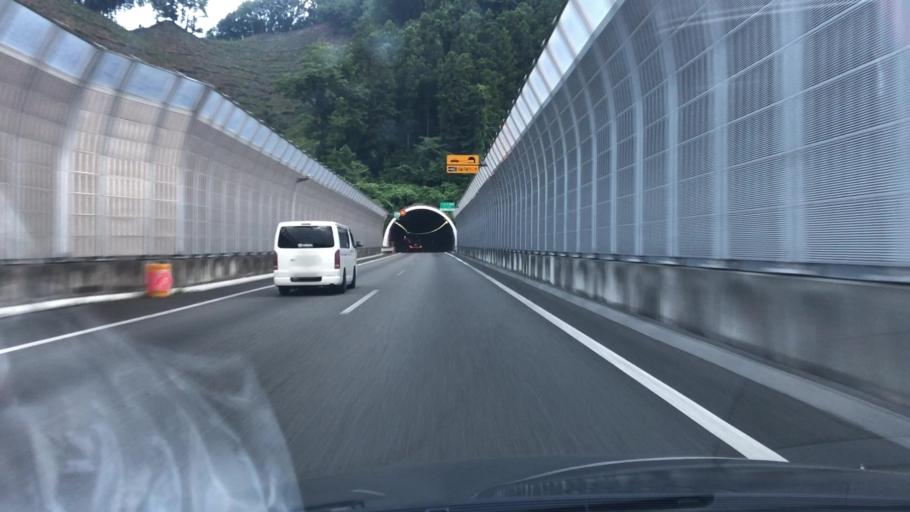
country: JP
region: Tokyo
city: Itsukaichi
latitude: 35.6653
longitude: 139.2501
